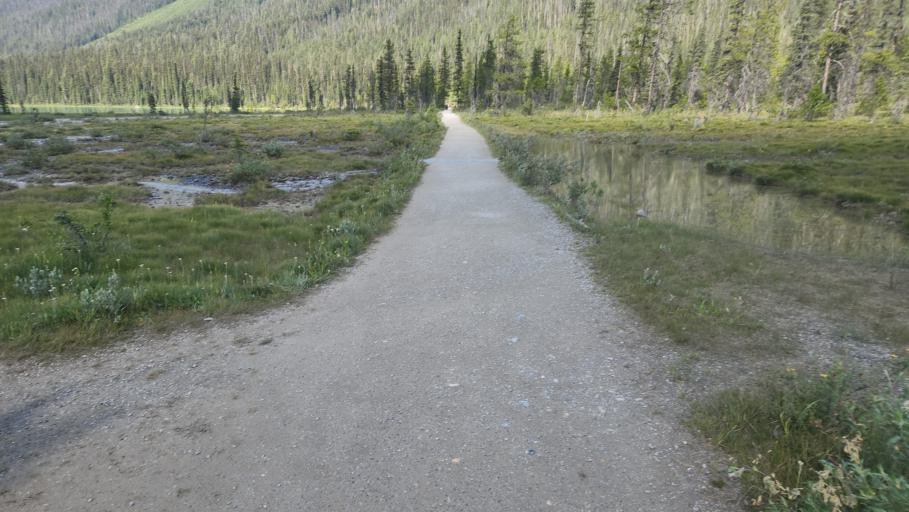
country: CA
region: Alberta
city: Lake Louise
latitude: 51.4510
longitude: -116.5253
